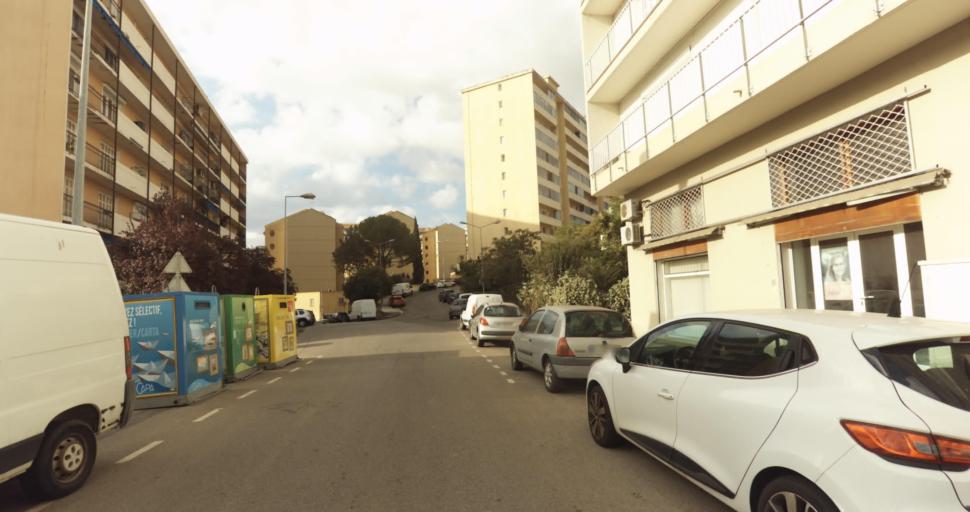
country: FR
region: Corsica
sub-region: Departement de la Corse-du-Sud
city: Ajaccio
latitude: 41.9304
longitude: 8.7350
